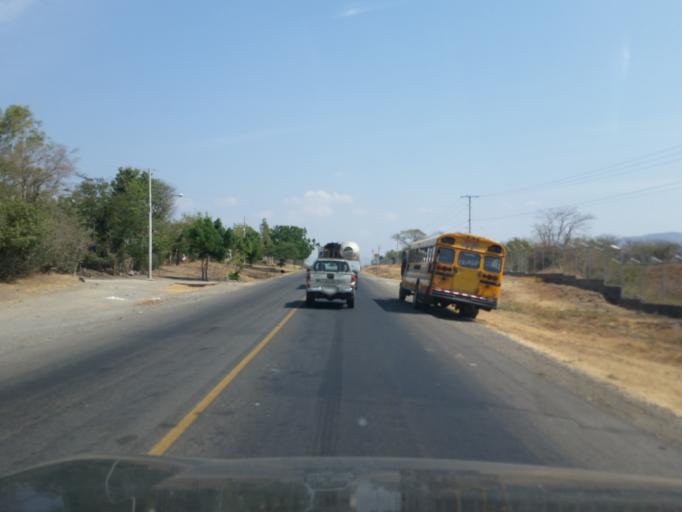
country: NI
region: Managua
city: Tipitapa
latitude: 12.3584
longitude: -86.0484
